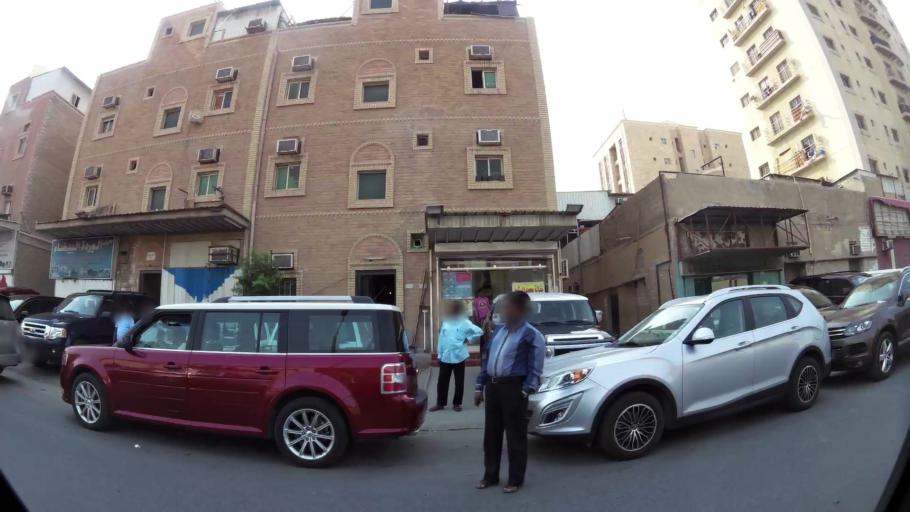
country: KW
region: Al Farwaniyah
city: Janub as Surrah
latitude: 29.2865
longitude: 47.9749
